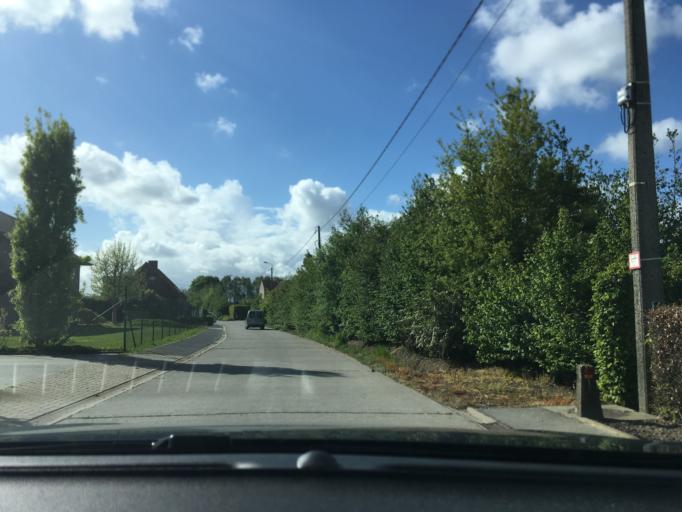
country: BE
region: Flanders
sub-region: Provincie West-Vlaanderen
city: Hooglede
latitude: 50.9988
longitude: 3.0806
